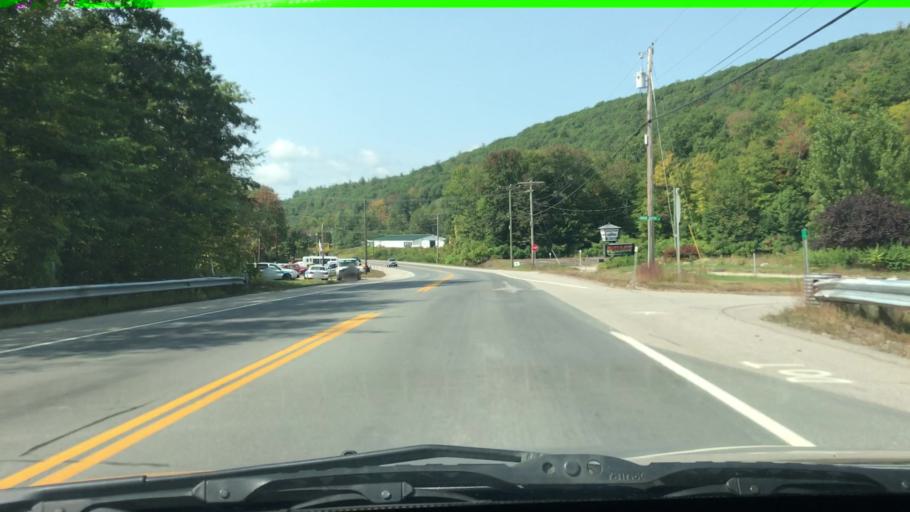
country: US
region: New Hampshire
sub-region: Cheshire County
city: Marlborough
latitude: 42.8724
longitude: -72.2154
